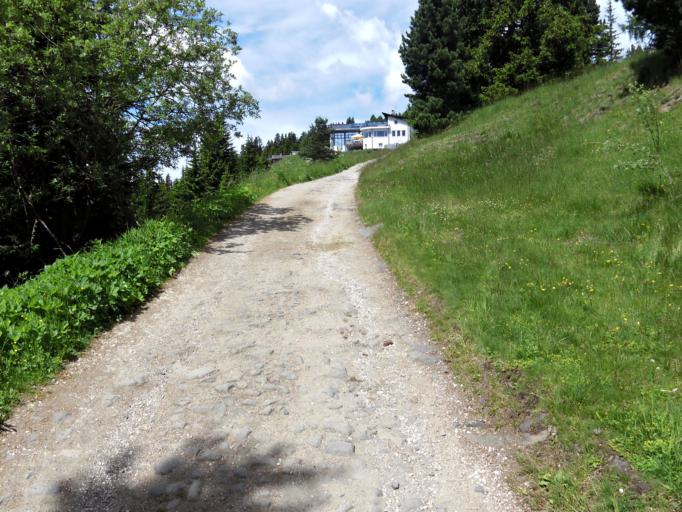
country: IT
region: Trentino-Alto Adige
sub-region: Bolzano
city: Ortisei
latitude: 46.5579
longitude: 11.6672
